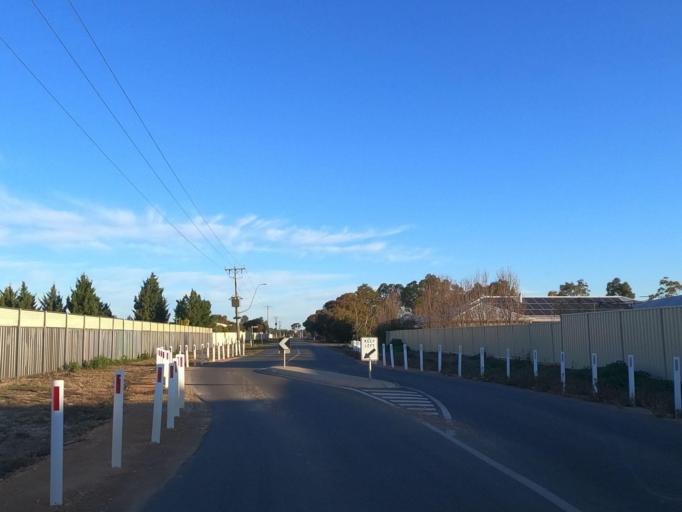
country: AU
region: Victoria
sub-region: Swan Hill
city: Swan Hill
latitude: -35.3292
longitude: 143.5348
